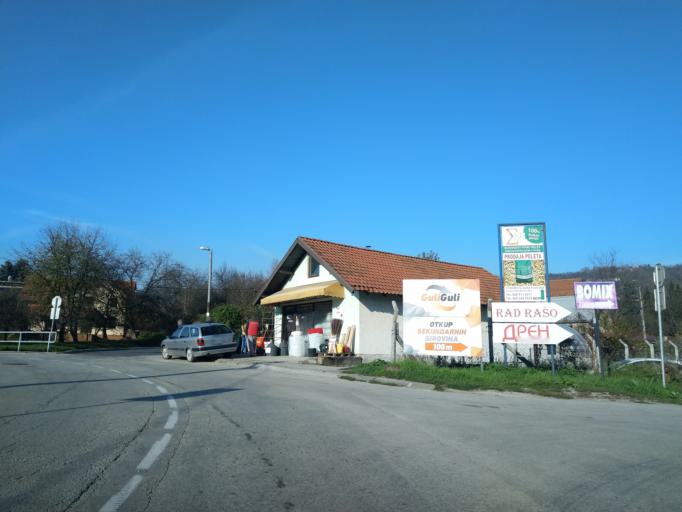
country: RS
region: Central Serbia
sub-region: Zlatiborski Okrug
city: Uzice
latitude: 43.8422
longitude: 19.8994
